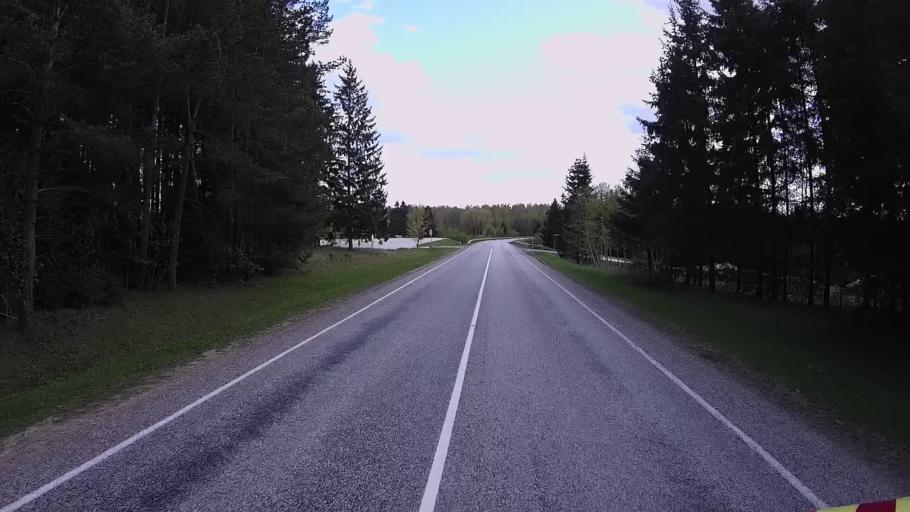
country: EE
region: Jogevamaa
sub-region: Jogeva linn
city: Jogeva
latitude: 58.7785
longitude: 26.4730
